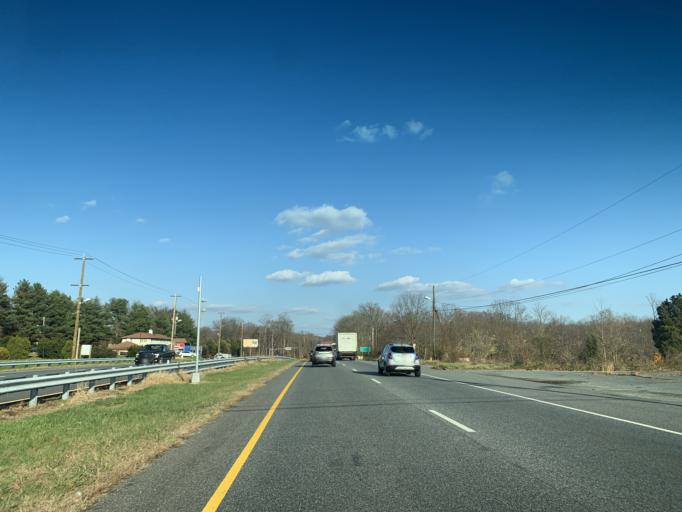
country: US
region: Maryland
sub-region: Cecil County
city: Perryville
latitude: 39.5729
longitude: -76.0629
